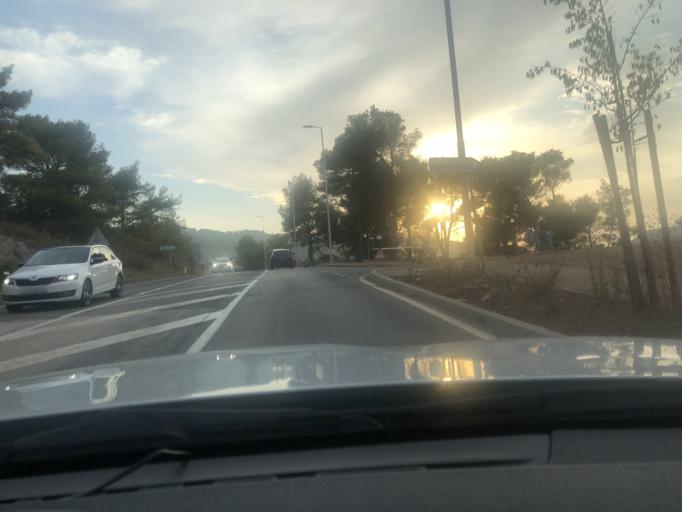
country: HR
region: Splitsko-Dalmatinska
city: Stari Grad
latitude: 43.1801
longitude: 16.5744
